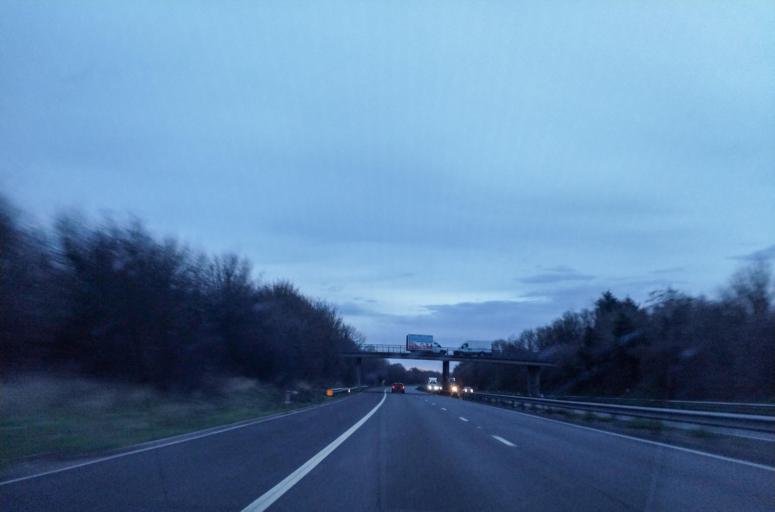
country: GB
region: England
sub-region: Kent
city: Newington
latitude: 51.3209
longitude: 0.6874
